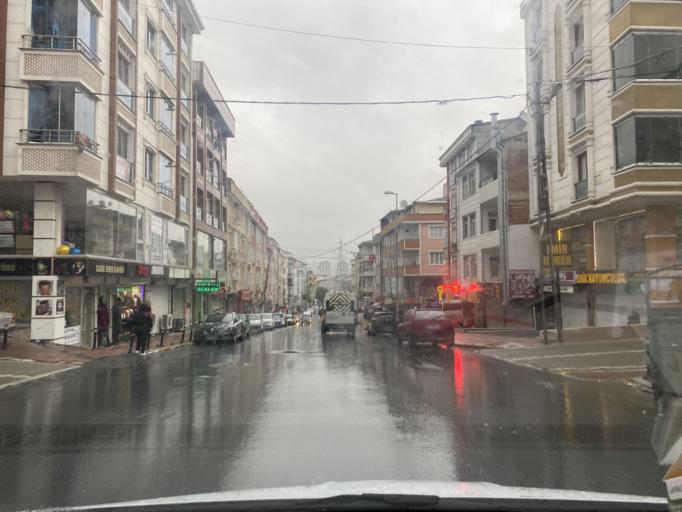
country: TR
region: Istanbul
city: Esenyurt
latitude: 41.0213
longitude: 28.6649
